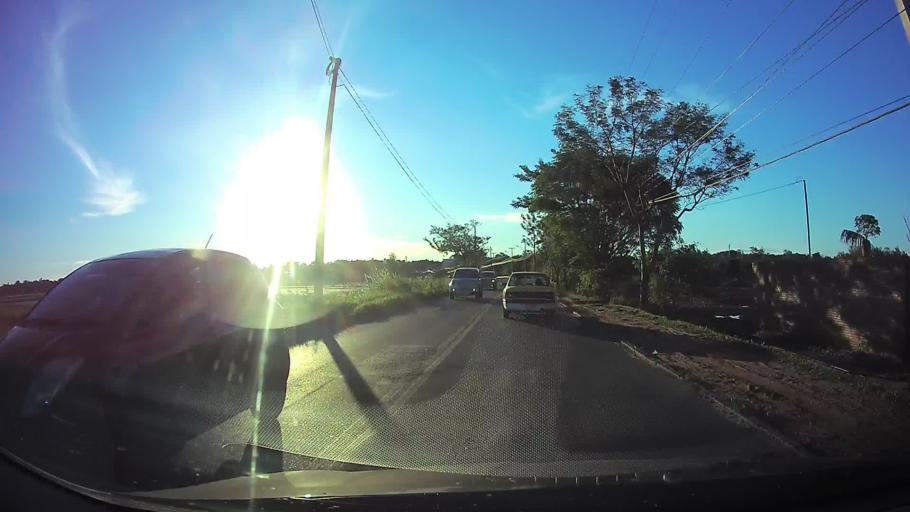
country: PY
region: Central
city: Limpio
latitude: -25.2143
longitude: -57.5075
